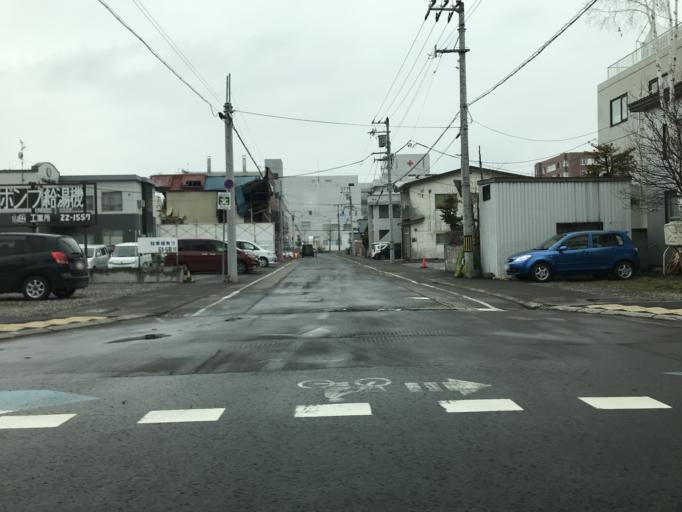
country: JP
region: Hokkaido
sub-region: Asahikawa-shi
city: Asahikawa
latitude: 43.7688
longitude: 142.3503
